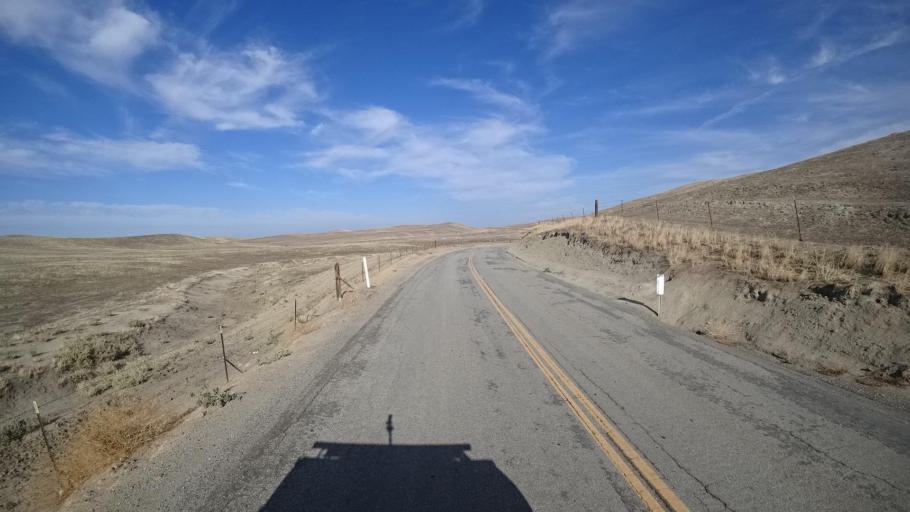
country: US
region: California
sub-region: Kern County
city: Oildale
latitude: 35.6228
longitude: -118.9877
